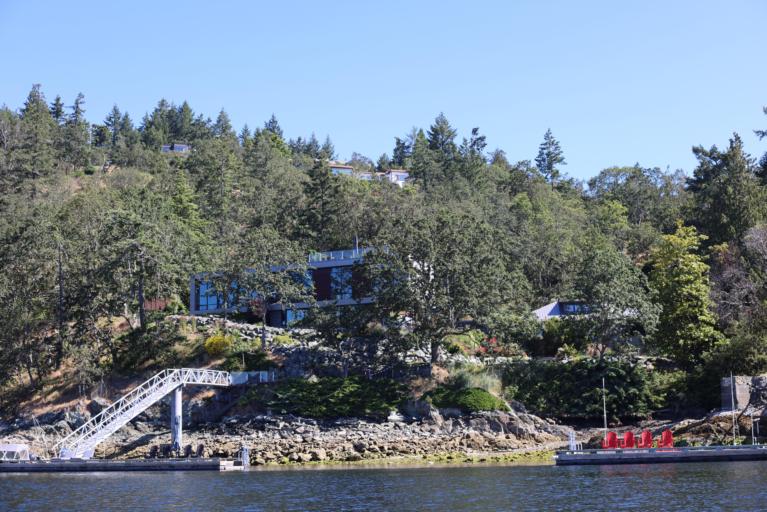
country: CA
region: British Columbia
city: North Cowichan
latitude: 48.8207
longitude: -123.5917
